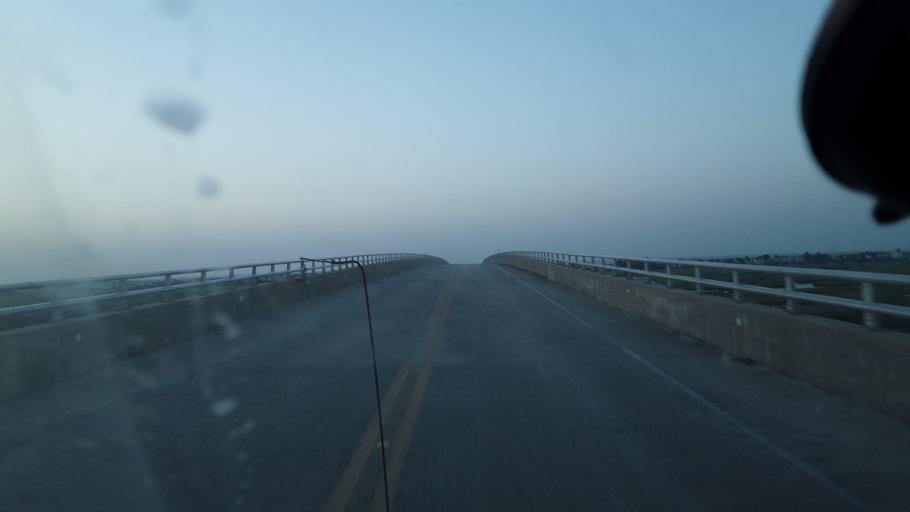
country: US
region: North Carolina
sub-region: Brunswick County
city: Sunset Beach
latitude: 33.8824
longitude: -78.5122
